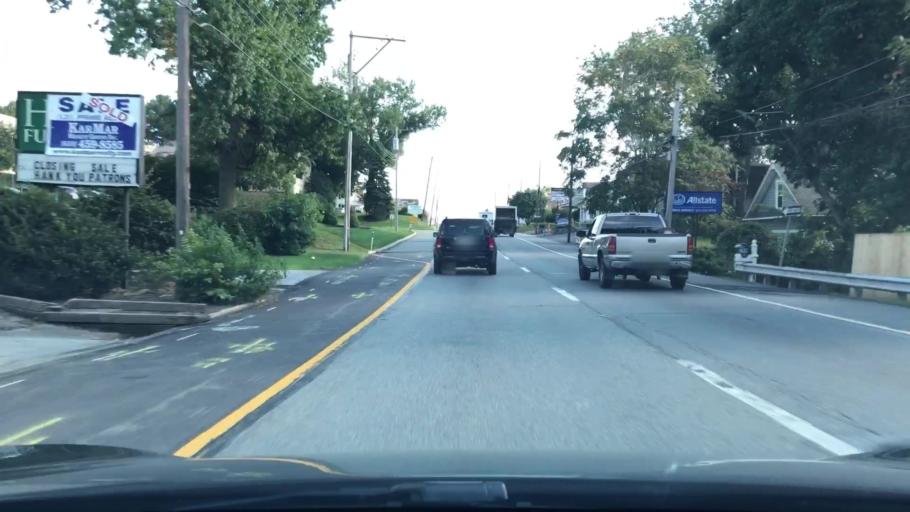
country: US
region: Pennsylvania
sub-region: Delaware County
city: Chester Heights
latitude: 39.8544
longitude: -75.5409
